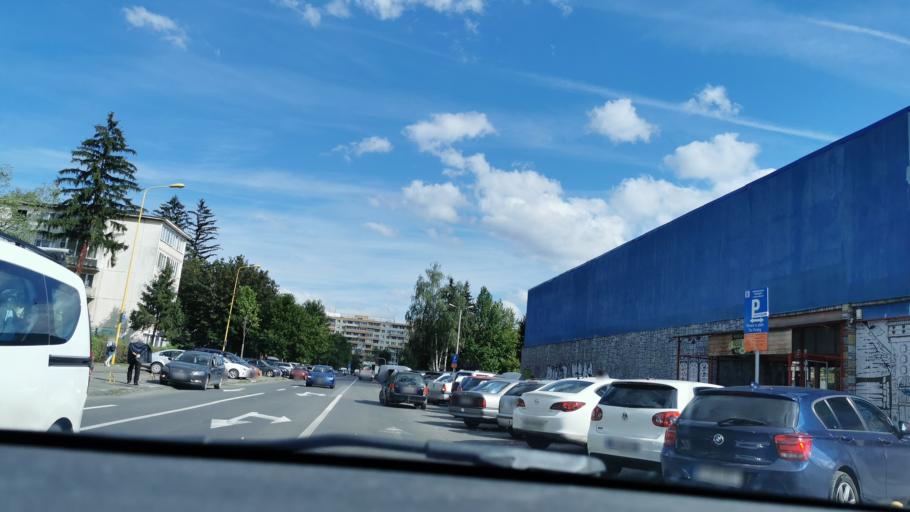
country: RO
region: Brasov
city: Brasov
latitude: 45.6428
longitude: 25.6291
